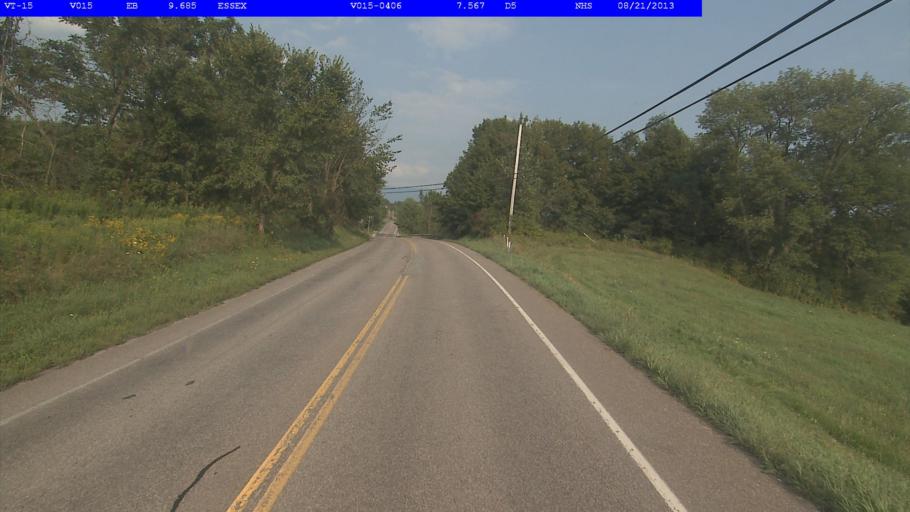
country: US
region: Vermont
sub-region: Chittenden County
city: Jericho
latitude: 44.5024
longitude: -73.0181
